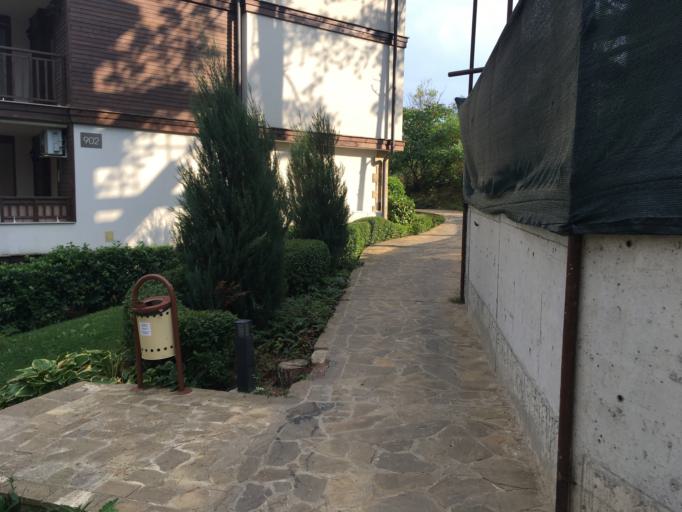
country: BG
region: Burgas
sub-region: Obshtina Sozopol
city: Sozopol
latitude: 42.4111
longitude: 27.6822
